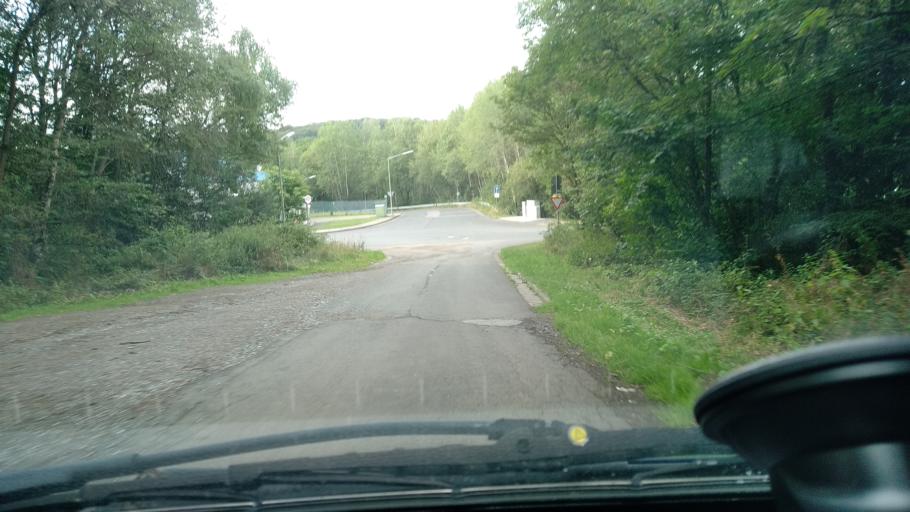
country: DE
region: North Rhine-Westphalia
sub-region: Regierungsbezirk Arnsberg
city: Burbach
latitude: 50.7541
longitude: 8.1149
